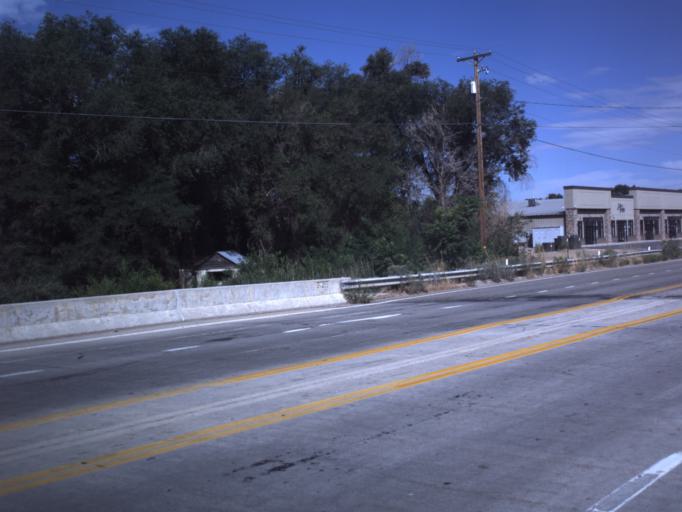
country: US
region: Utah
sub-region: Box Elder County
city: South Willard
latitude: 41.3480
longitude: -112.0340
